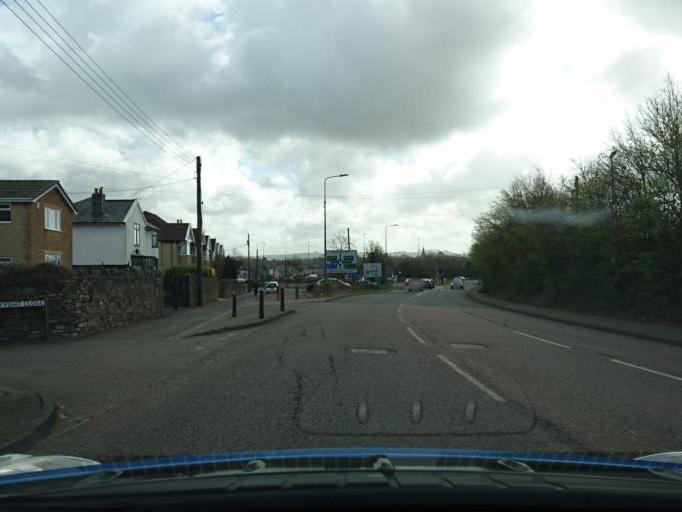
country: GB
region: England
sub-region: South Gloucestershire
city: Kingswood
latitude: 51.4603
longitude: -2.4851
